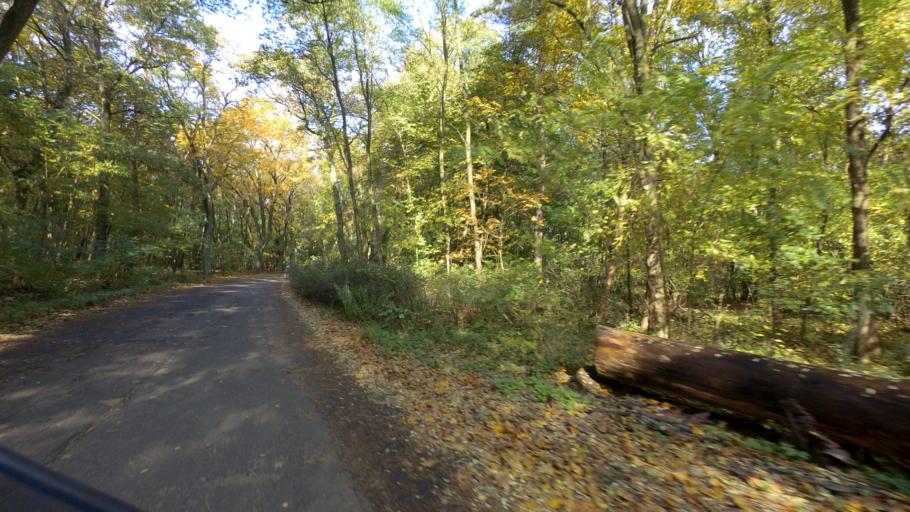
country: DE
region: Berlin
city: Friedrichshagen
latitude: 52.4266
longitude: 13.6157
